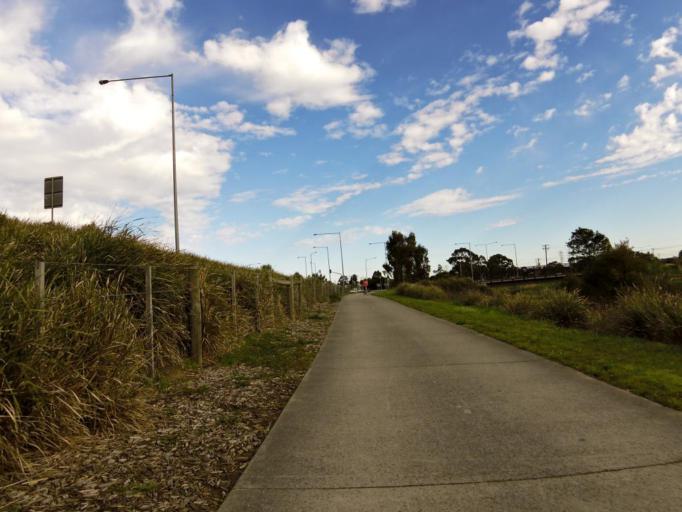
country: AU
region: Victoria
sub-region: Knox
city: Wantirna South
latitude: -37.9021
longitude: 145.2143
